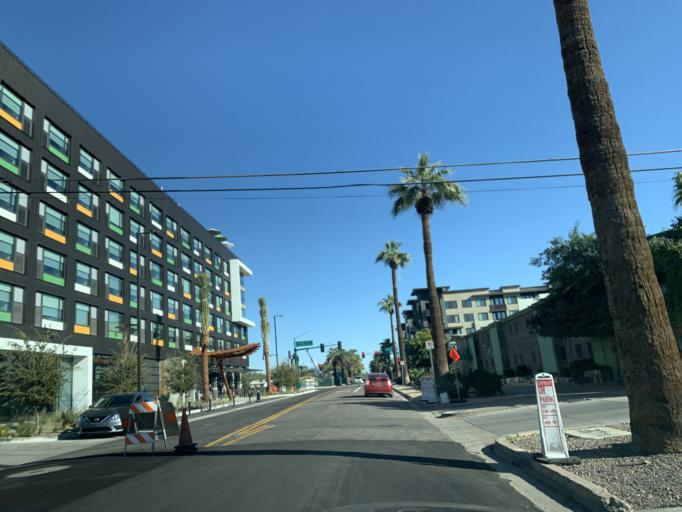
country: US
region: Arizona
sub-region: Maricopa County
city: Phoenix
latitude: 33.4600
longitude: -112.0706
